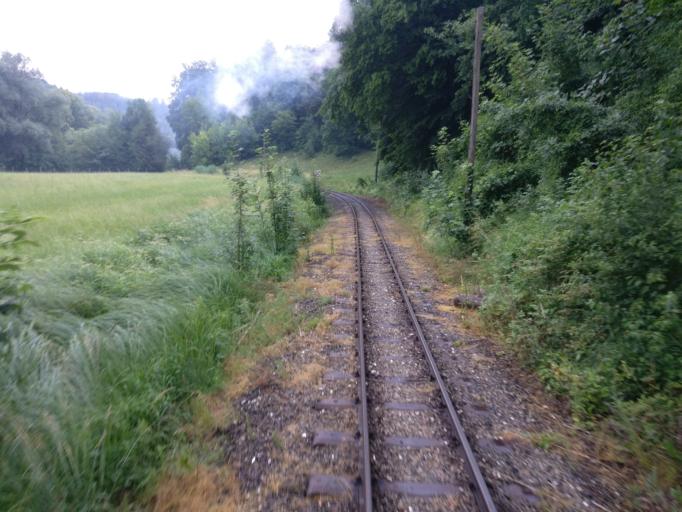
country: AT
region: Upper Austria
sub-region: Politischer Bezirk Steyr-Land
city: Waldneukirchen
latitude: 47.9913
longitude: 14.2806
